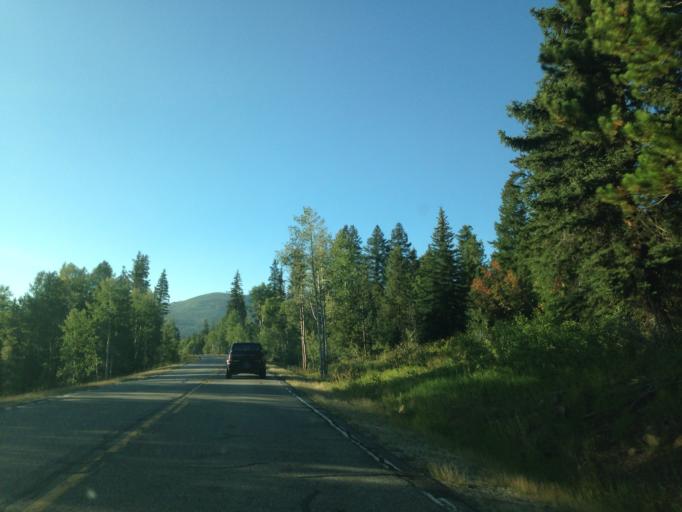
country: US
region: Utah
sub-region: Summit County
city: Francis
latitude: 40.6071
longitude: -111.1210
